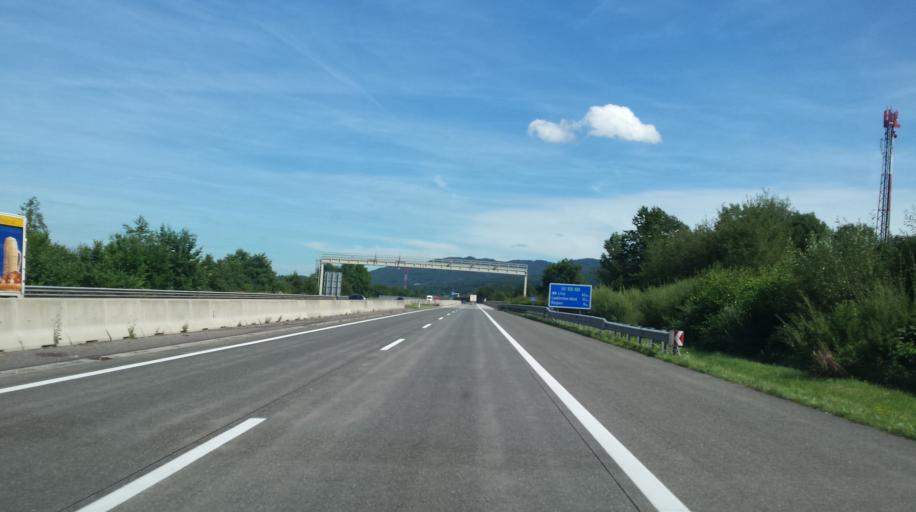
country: AT
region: Upper Austria
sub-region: Politischer Bezirk Vocklabruck
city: Seewalchen
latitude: 47.9532
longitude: 13.6022
